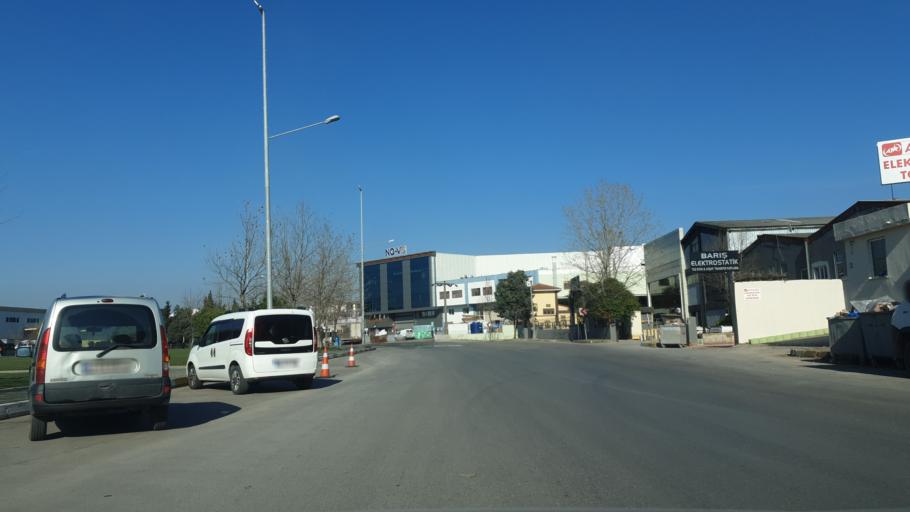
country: TR
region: Kocaeli
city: Balcik
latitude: 40.8772
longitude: 29.3660
